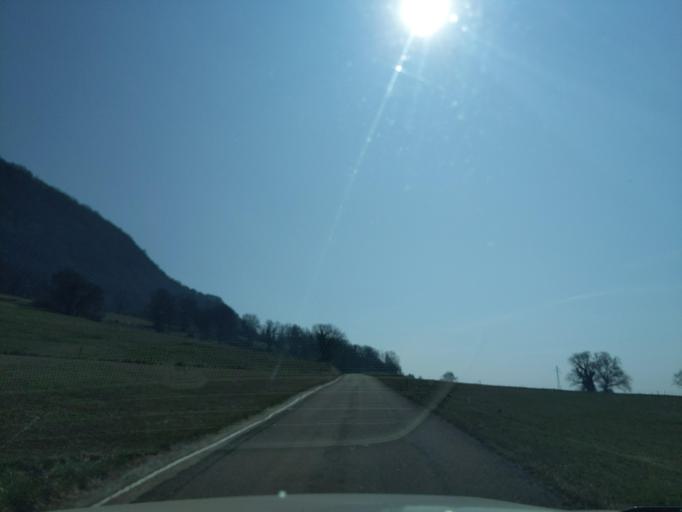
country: FR
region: Rhone-Alpes
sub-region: Departement de la Haute-Savoie
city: Versonnex
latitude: 45.9264
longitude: 5.8460
